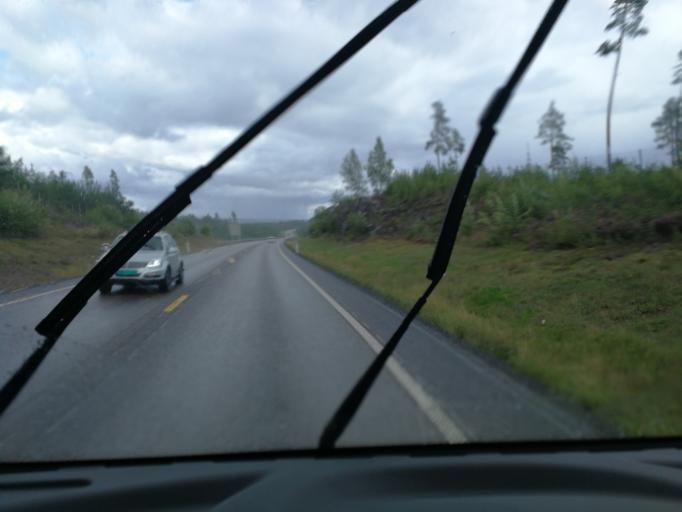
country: NO
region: Ostfold
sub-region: Marker
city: Orje
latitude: 59.5383
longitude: 11.5484
